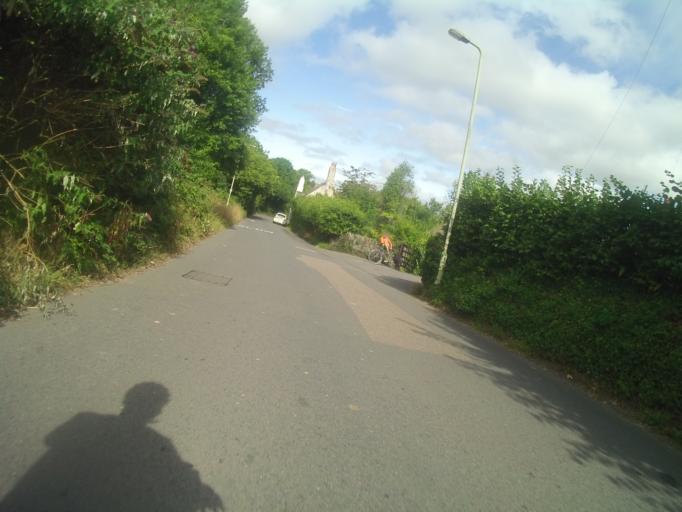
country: GB
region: England
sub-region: Devon
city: Totnes
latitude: 50.4412
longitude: -3.7069
